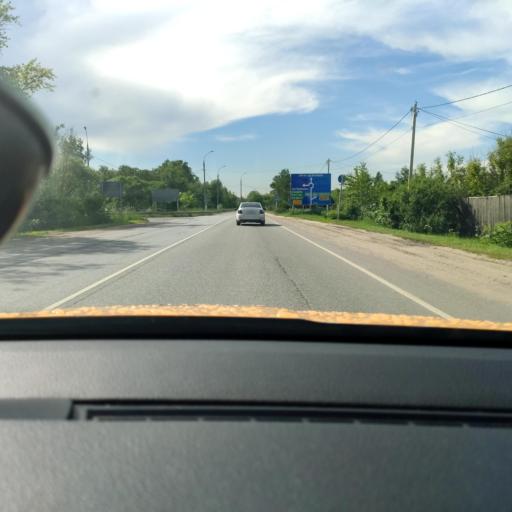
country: RU
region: Moskovskaya
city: Zhilevo
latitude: 54.9667
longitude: 37.9799
